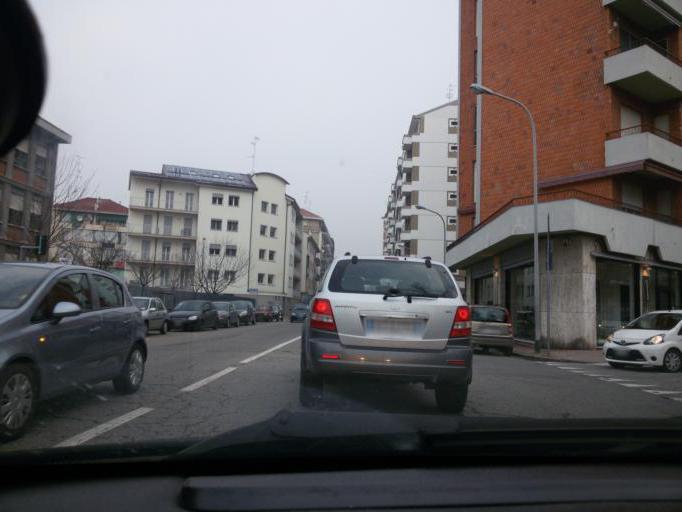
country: IT
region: Piedmont
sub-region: Provincia di Vercelli
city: Vercelli
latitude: 45.3185
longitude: 8.4125
